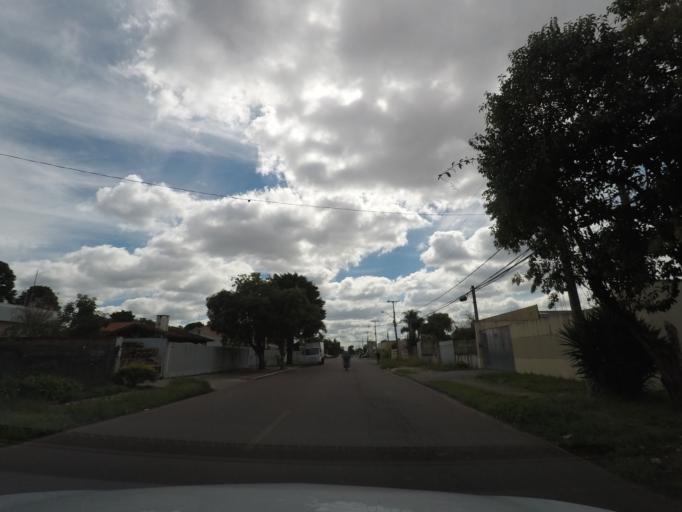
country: BR
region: Parana
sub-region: Sao Jose Dos Pinhais
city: Sao Jose dos Pinhais
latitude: -25.4842
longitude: -49.2420
